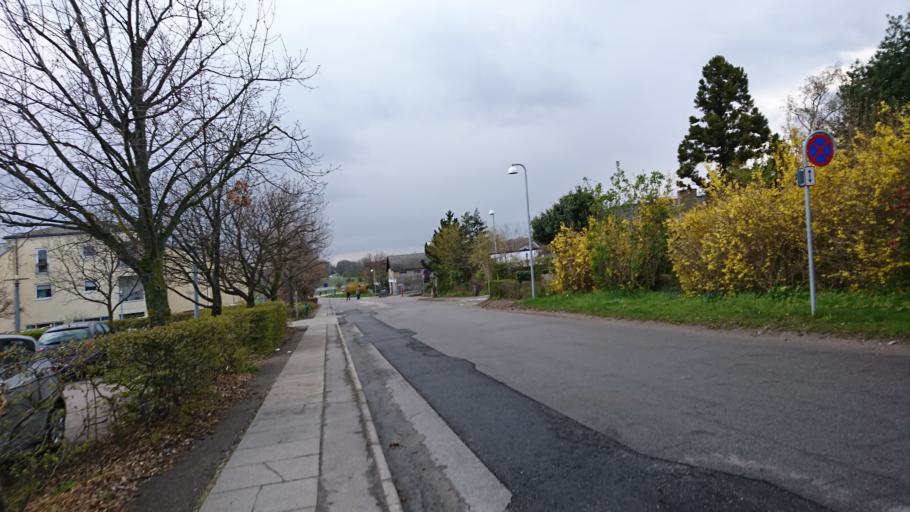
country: DK
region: Zealand
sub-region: Roskilde Kommune
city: Roskilde
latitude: 55.6679
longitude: 12.0932
